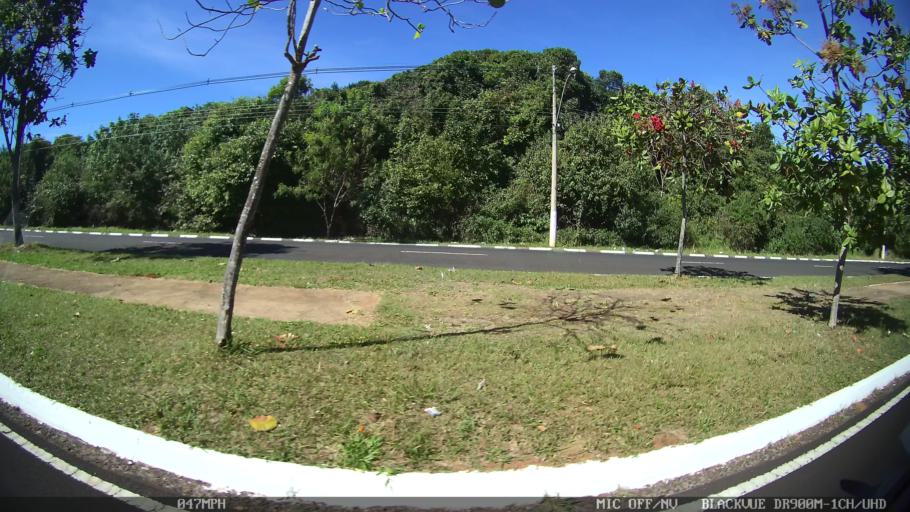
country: BR
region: Sao Paulo
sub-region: Franca
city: Franca
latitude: -20.5308
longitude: -47.3740
